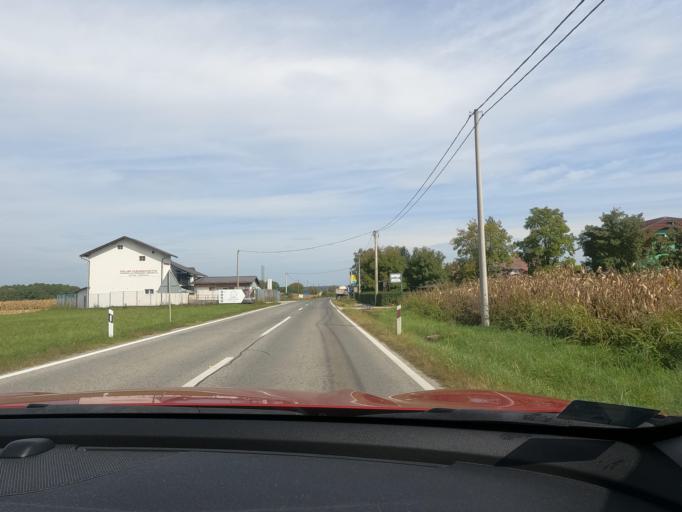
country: HR
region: Sisacko-Moslavacka
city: Osekovo
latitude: 45.5499
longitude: 16.5912
